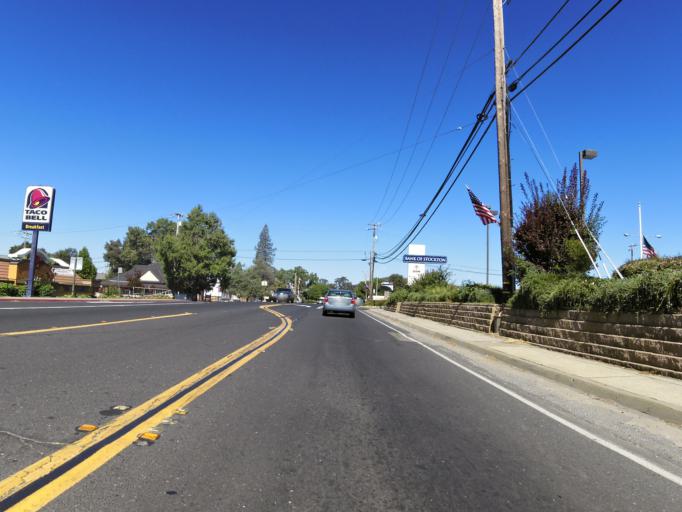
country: US
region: California
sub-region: Calaveras County
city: Angels Camp
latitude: 38.0799
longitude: -120.5552
